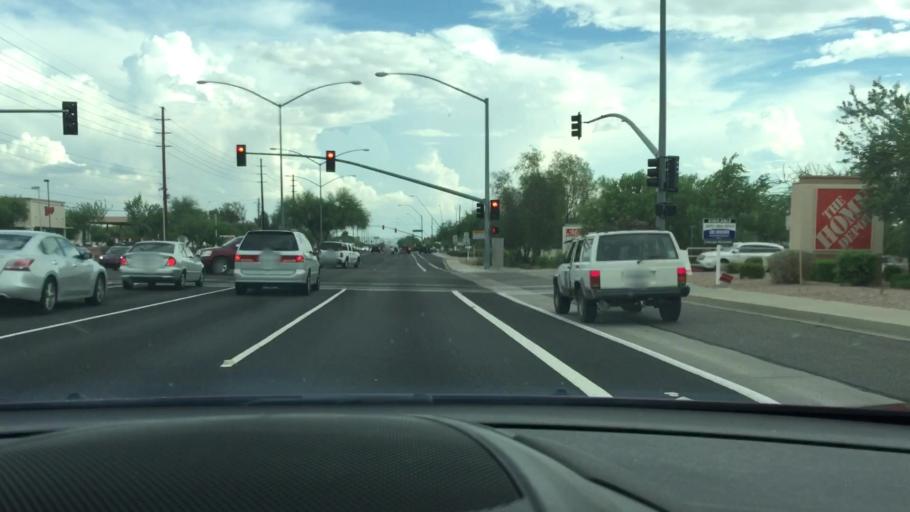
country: US
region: Arizona
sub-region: Pinal County
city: Apache Junction
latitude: 33.4539
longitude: -111.6843
